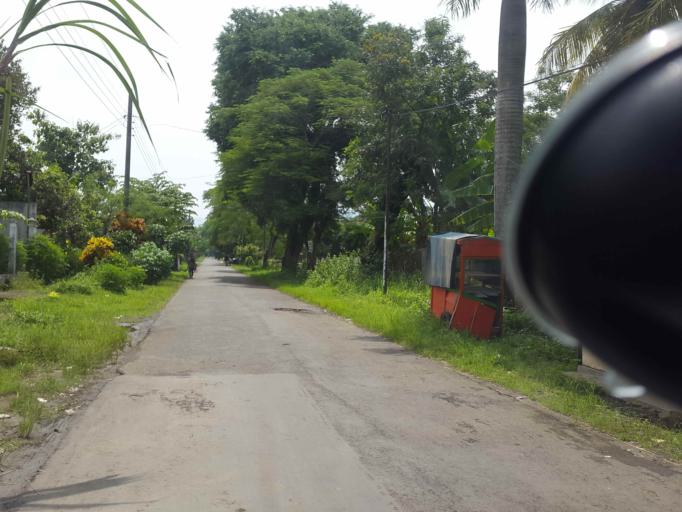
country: ID
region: Central Java
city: Banyumas
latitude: -7.5139
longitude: 109.2964
